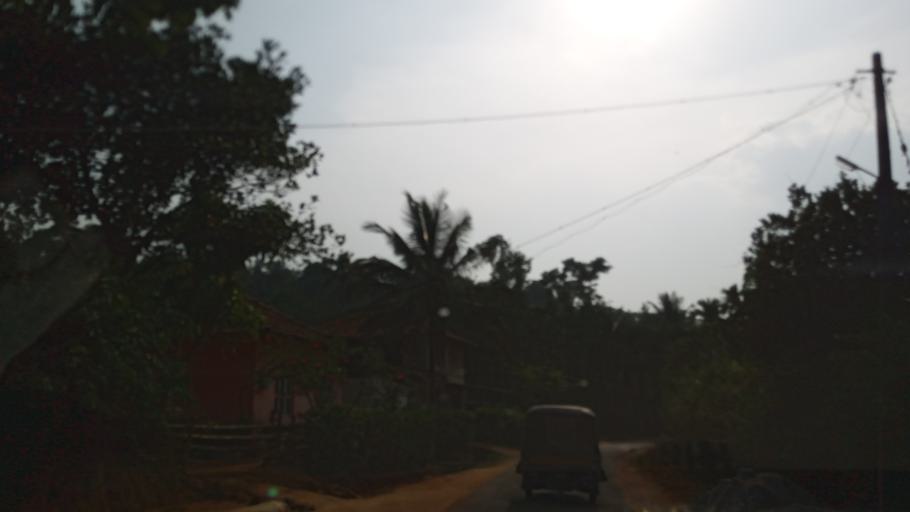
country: IN
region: Karnataka
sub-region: Chikmagalur
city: Mudigere
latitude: 13.0588
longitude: 75.6658
